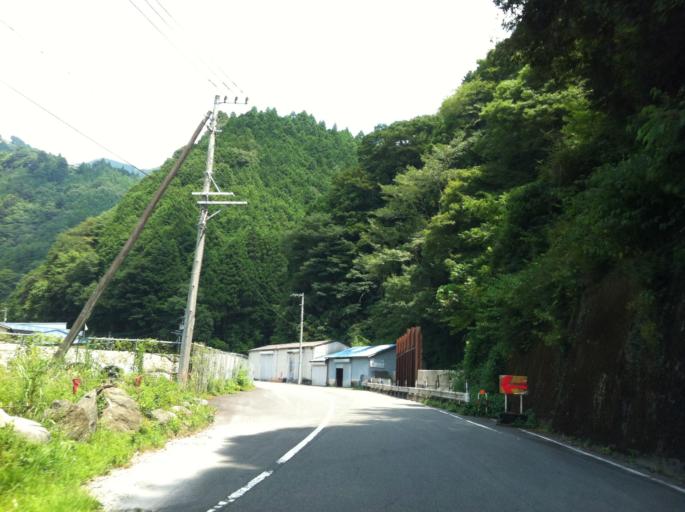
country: JP
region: Shizuoka
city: Shizuoka-shi
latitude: 35.2449
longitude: 138.3443
